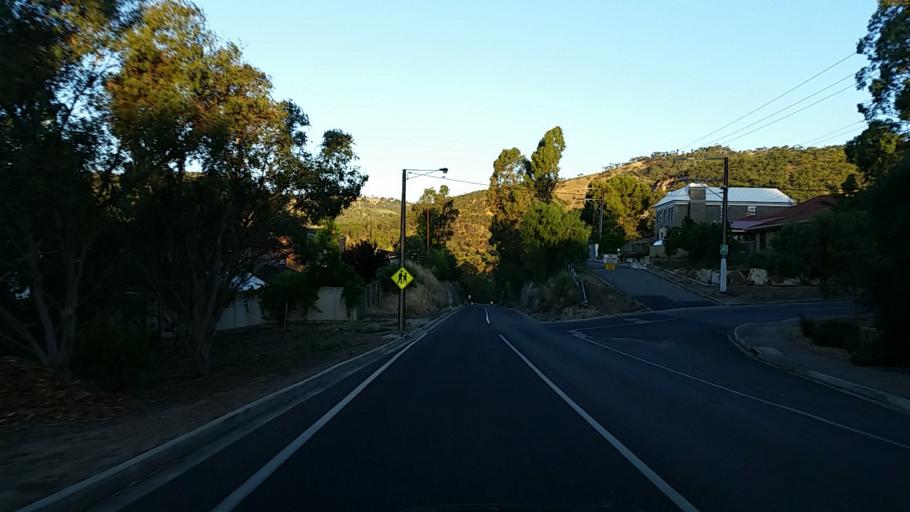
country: AU
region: South Australia
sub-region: Campbelltown
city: Athelstone
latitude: -34.8640
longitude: 138.7142
